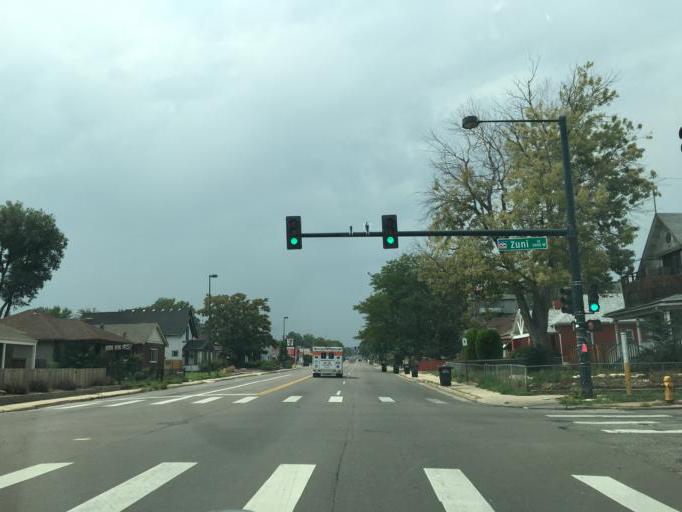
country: US
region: Colorado
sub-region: Adams County
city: Berkley
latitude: 39.7693
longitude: -105.0155
